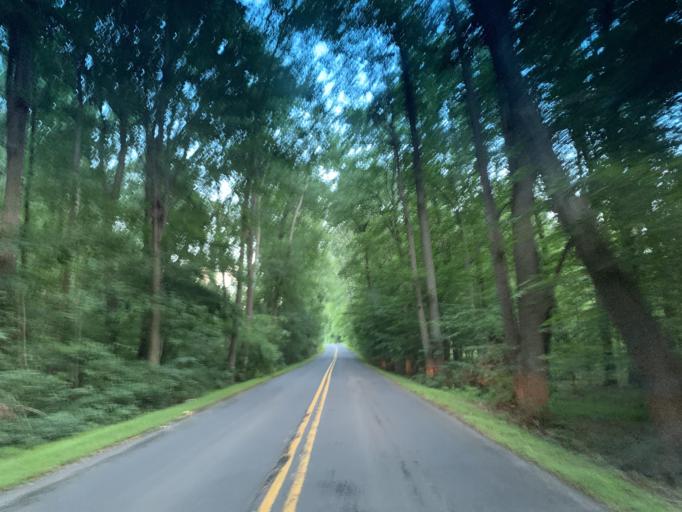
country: US
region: Maryland
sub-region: Harford County
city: Aberdeen
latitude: 39.5341
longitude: -76.1492
